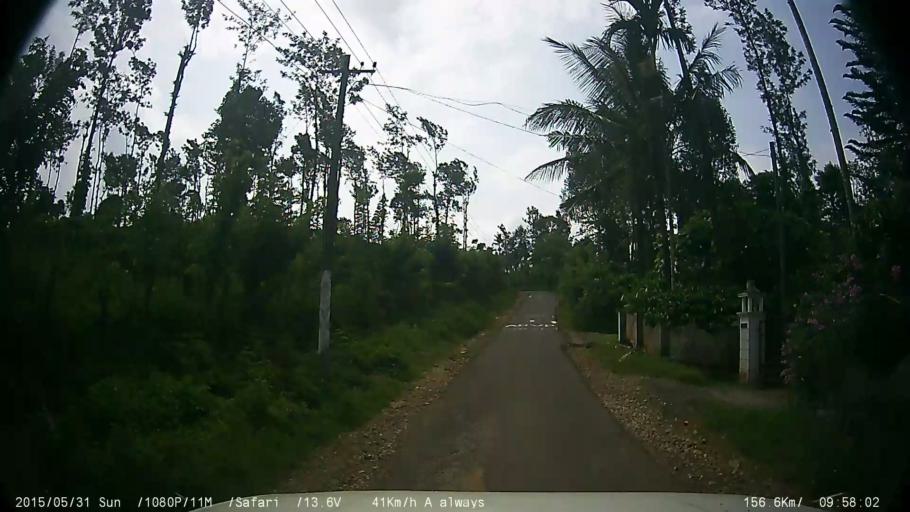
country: IN
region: Kerala
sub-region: Wayanad
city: Kalpetta
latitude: 11.5923
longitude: 76.0606
